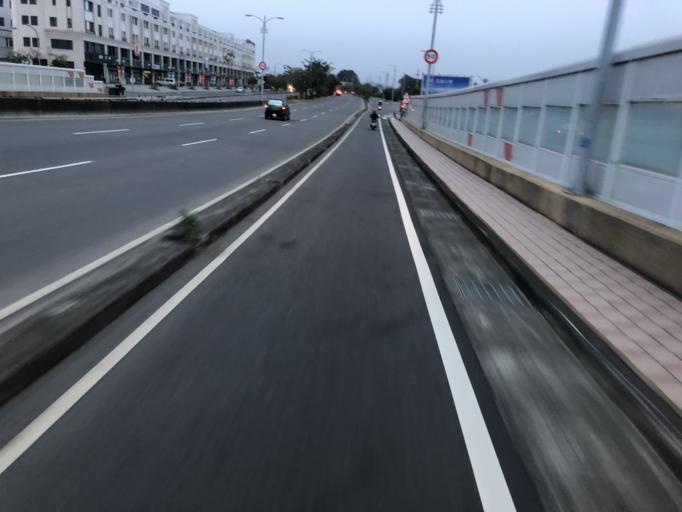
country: TW
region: Taiwan
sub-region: Tainan
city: Tainan
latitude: 23.1079
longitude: 120.3042
